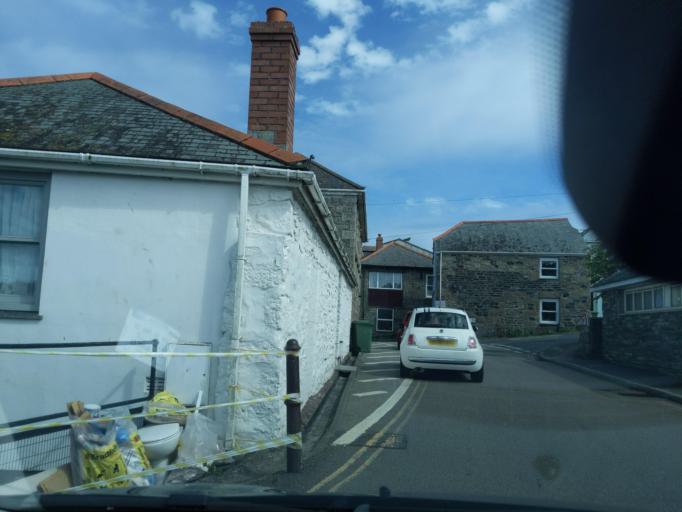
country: GB
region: England
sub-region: Cornwall
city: Penzance
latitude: 50.1022
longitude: -5.5477
